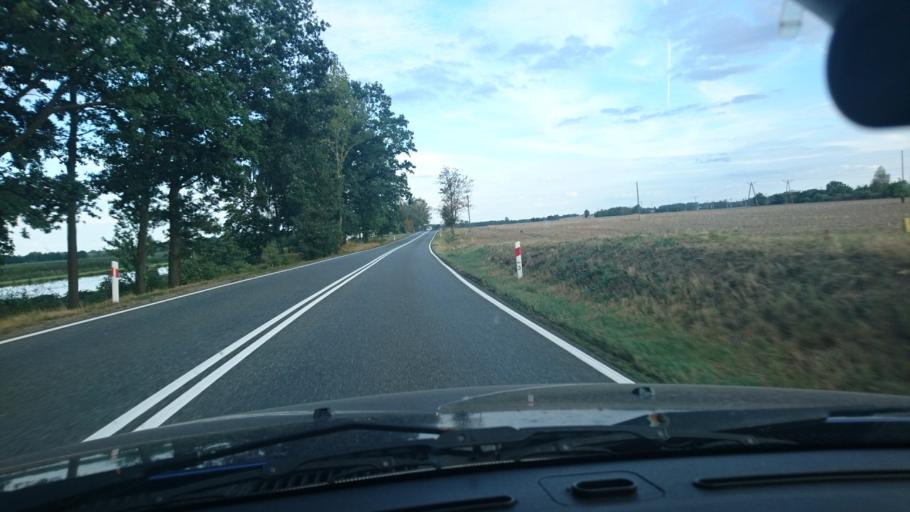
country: PL
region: Lodz Voivodeship
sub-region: Powiat wieruszowski
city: Boleslawiec
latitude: 51.1596
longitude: 18.1642
